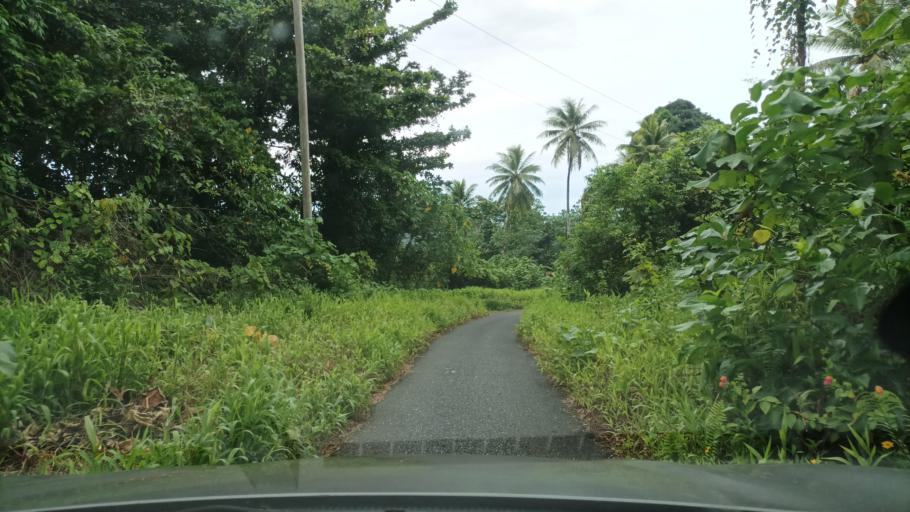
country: FM
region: Pohnpei
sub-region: Madolenihm Municipality
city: Madolenihm Municipality Government
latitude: 6.9137
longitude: 158.2882
